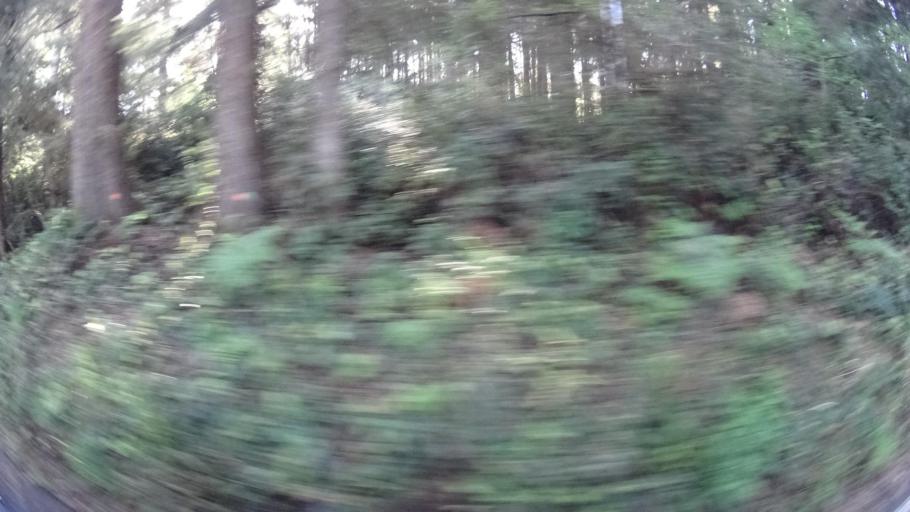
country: US
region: California
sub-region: Humboldt County
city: Westhaven-Moonstone
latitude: 41.1288
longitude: -124.1549
